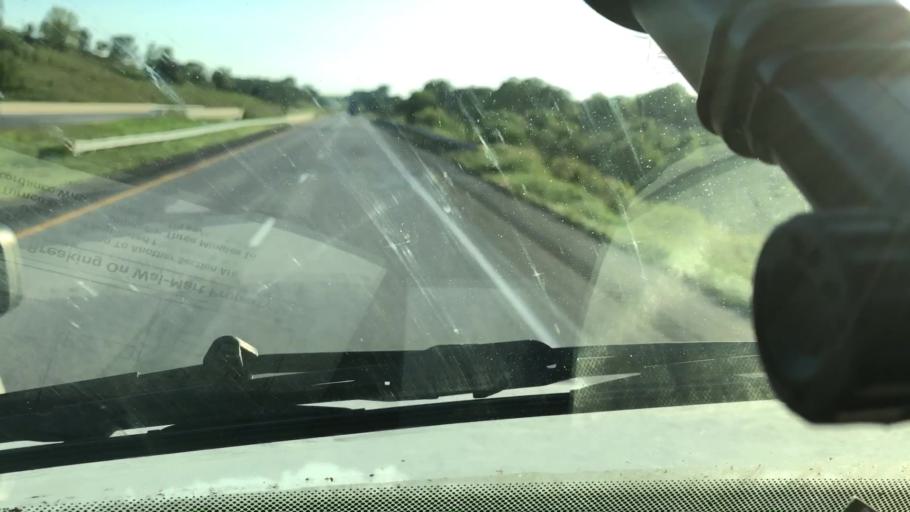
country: US
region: Iowa
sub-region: Pottawattamie County
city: Council Bluffs
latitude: 41.3376
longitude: -95.7346
